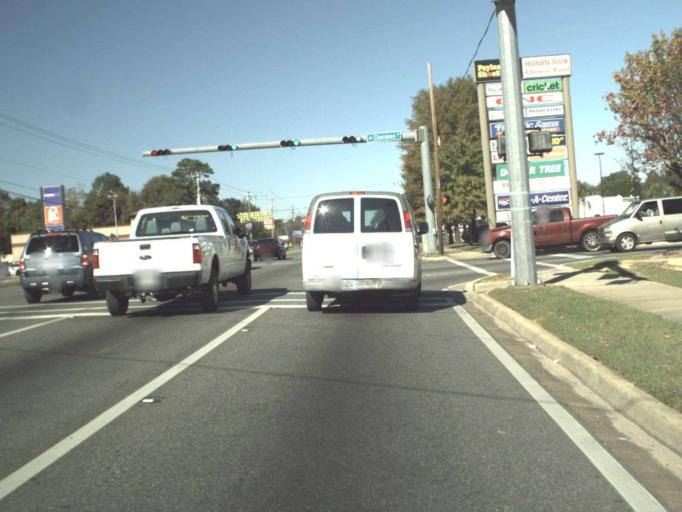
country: US
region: Florida
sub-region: Escambia County
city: West Pensacola
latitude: 30.4362
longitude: -87.2780
